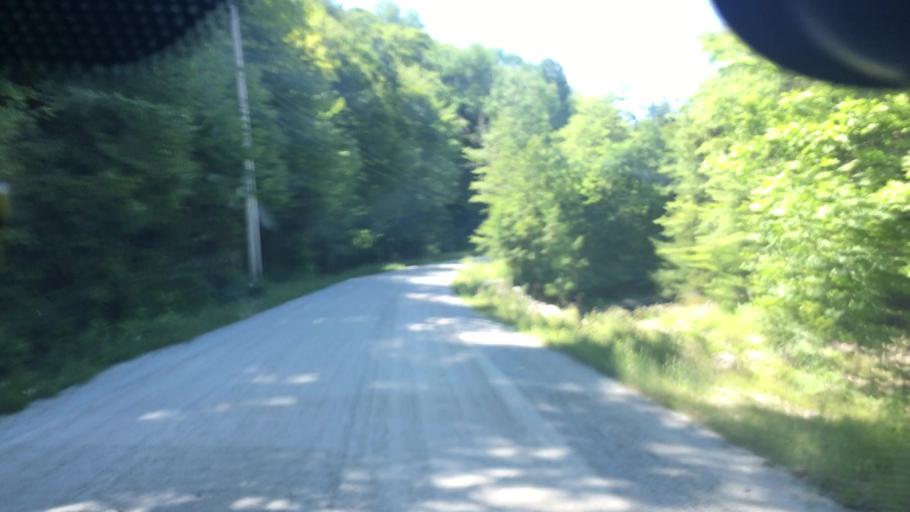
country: US
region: Vermont
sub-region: Windsor County
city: Chester
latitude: 43.4333
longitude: -72.7227
